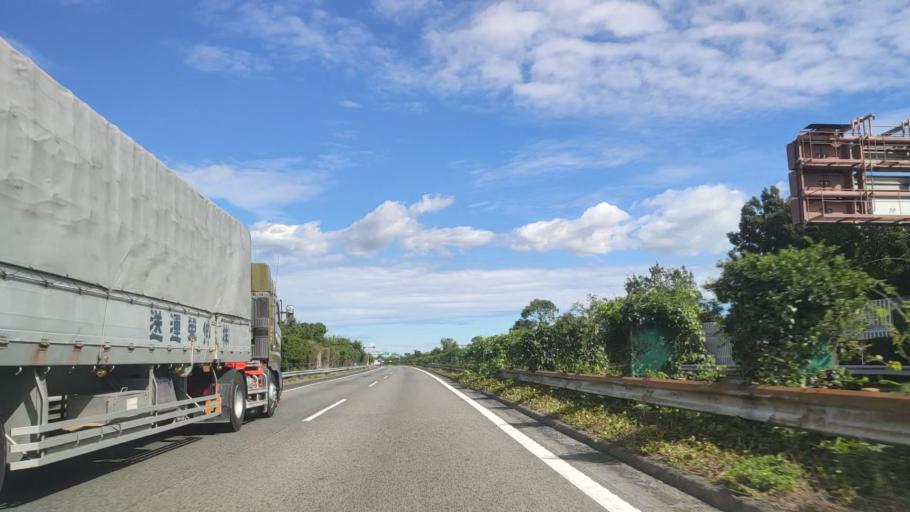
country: JP
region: Shizuoka
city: Hamamatsu
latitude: 34.7490
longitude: 137.7592
